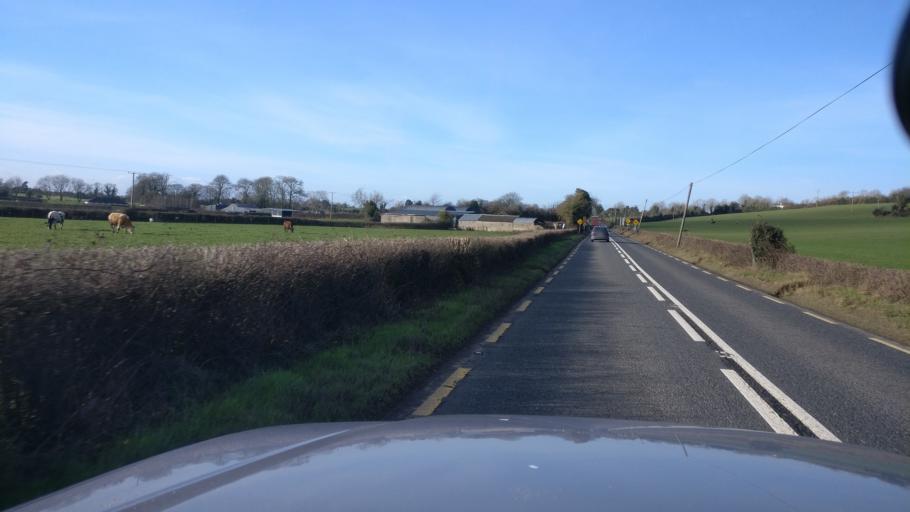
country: IE
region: Leinster
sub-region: Uibh Fhaili
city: Tullamore
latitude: 53.1949
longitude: -7.4149
